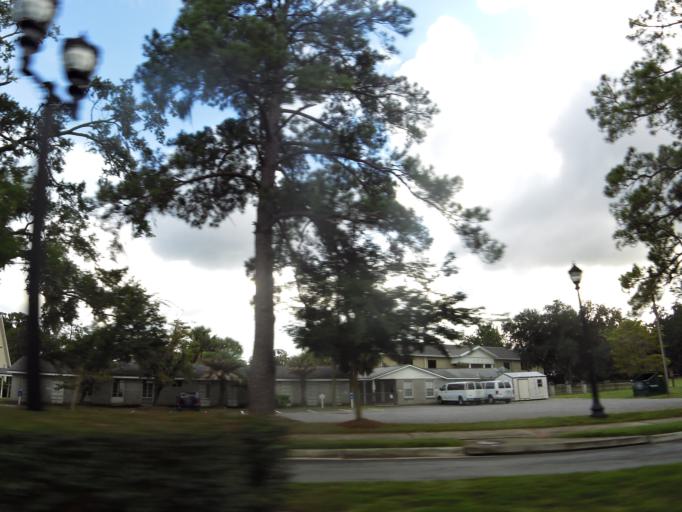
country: US
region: Georgia
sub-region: Liberty County
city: Hinesville
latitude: 31.8491
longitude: -81.5910
